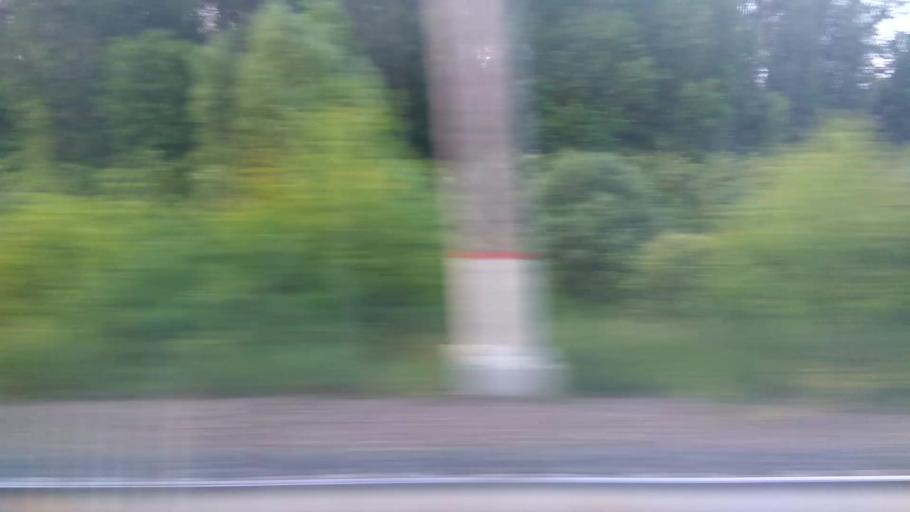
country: RU
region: Moskovskaya
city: Vostryakovo
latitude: 55.3906
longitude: 37.8086
